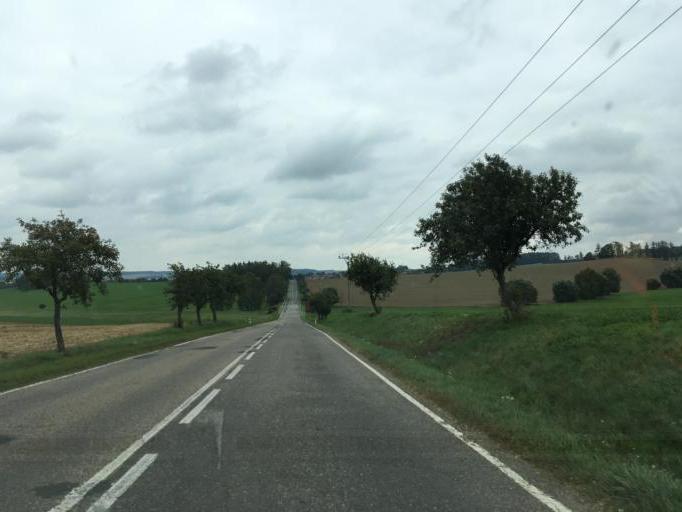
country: CZ
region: Central Bohemia
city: Cechtice
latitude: 49.6338
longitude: 15.0306
